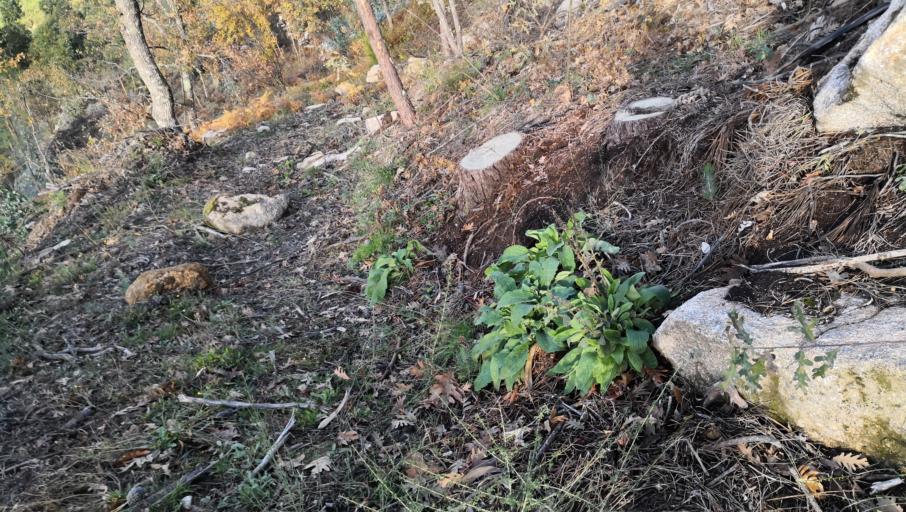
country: PT
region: Vila Real
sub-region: Vila Real
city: Vila Real
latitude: 41.3273
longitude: -7.7102
